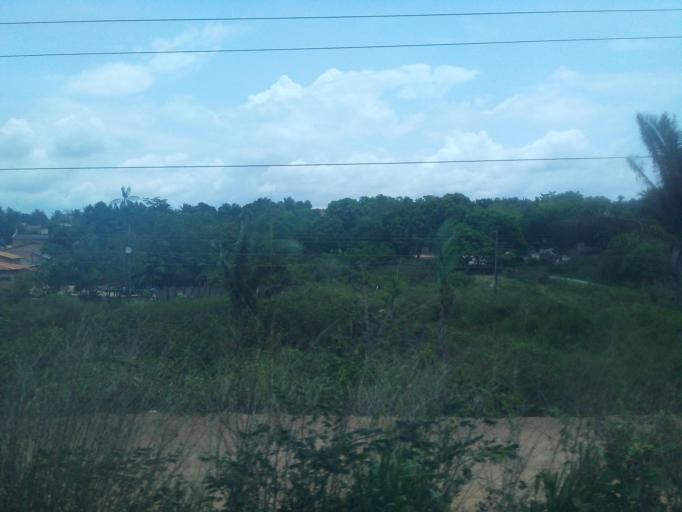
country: BR
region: Maranhao
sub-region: Santa Ines
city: Santa Ines
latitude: -3.7068
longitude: -45.5681
